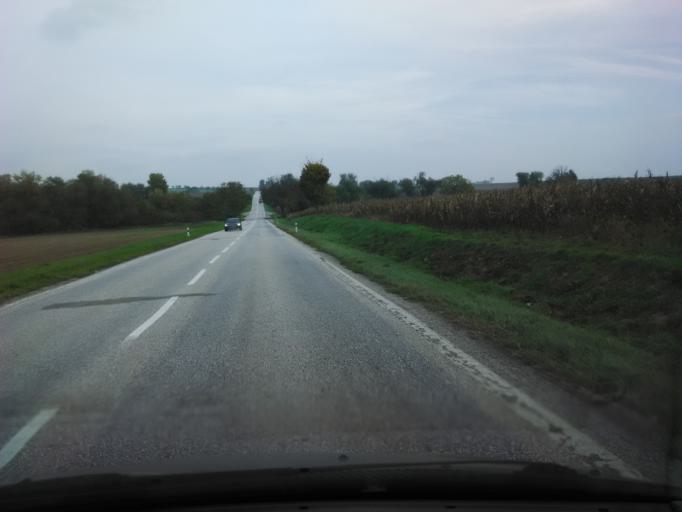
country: SK
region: Nitriansky
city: Svodin
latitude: 48.0003
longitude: 18.3558
